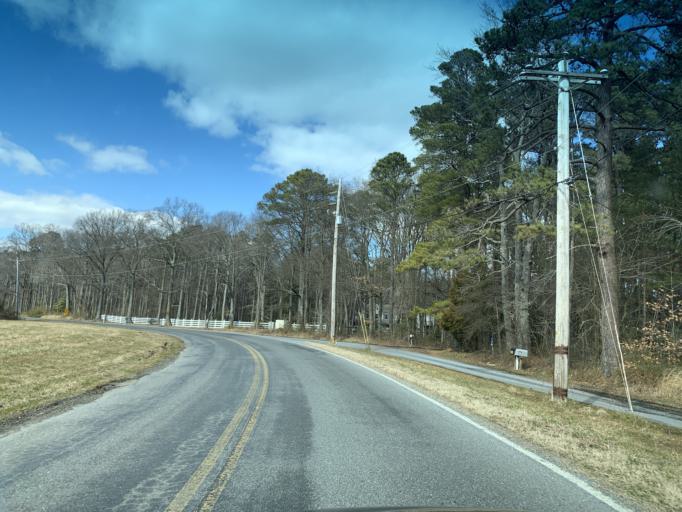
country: US
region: Maryland
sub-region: Queen Anne's County
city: Chester
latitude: 38.9424
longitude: -76.2659
